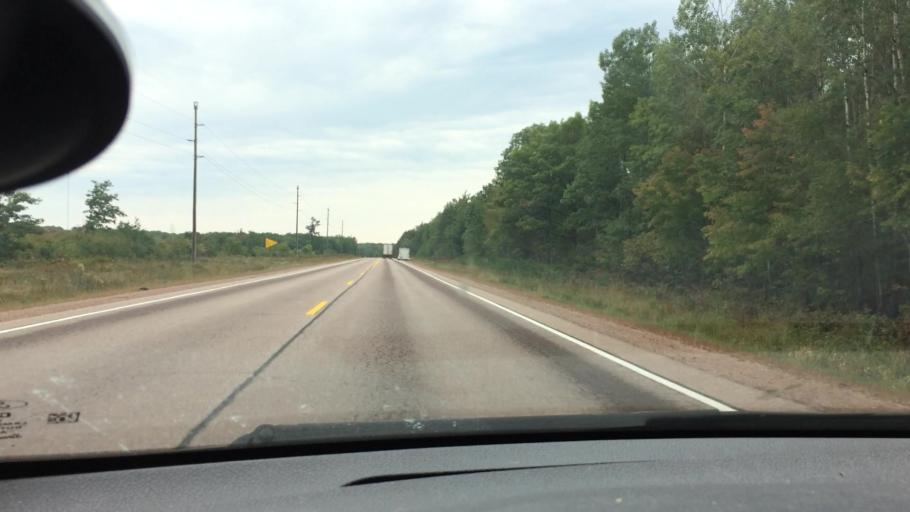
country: US
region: Wisconsin
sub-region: Clark County
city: Neillsville
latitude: 44.5874
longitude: -90.7563
